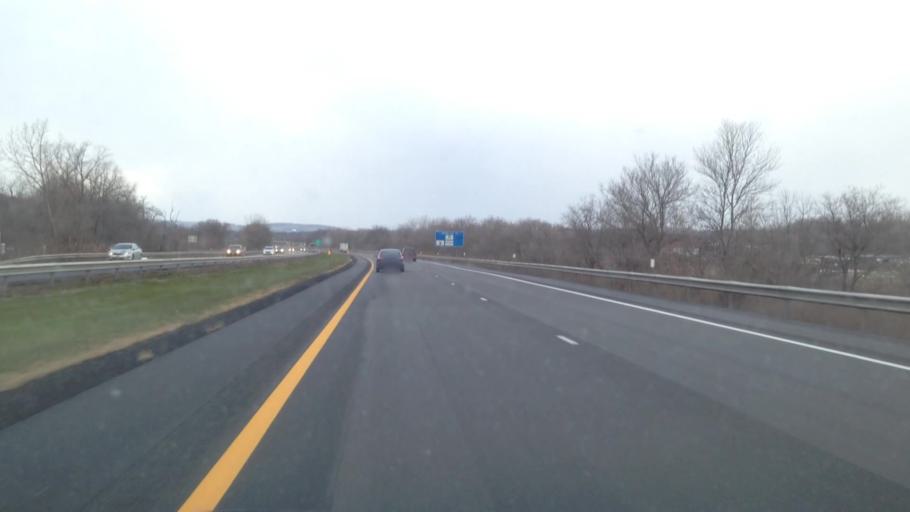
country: US
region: New York
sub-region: Montgomery County
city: Fonda
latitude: 42.9415
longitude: -74.3444
